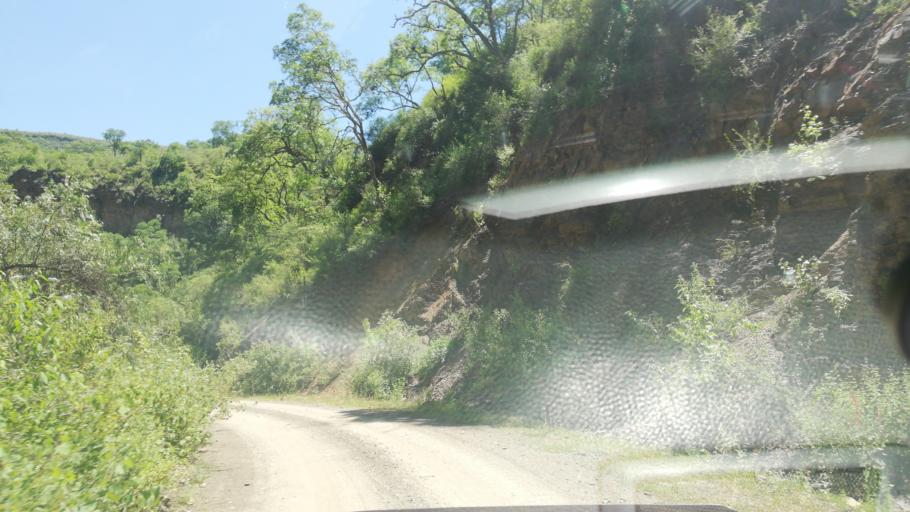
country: BO
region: Cochabamba
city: Mizque
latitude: -17.8355
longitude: -65.3092
